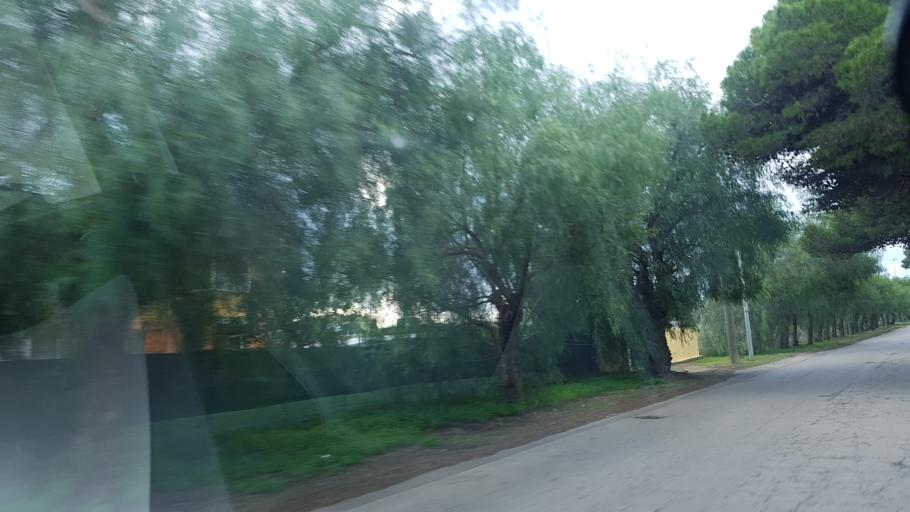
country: IT
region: Apulia
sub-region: Provincia di Brindisi
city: San Pietro Vernotico
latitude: 40.4879
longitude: 18.0044
